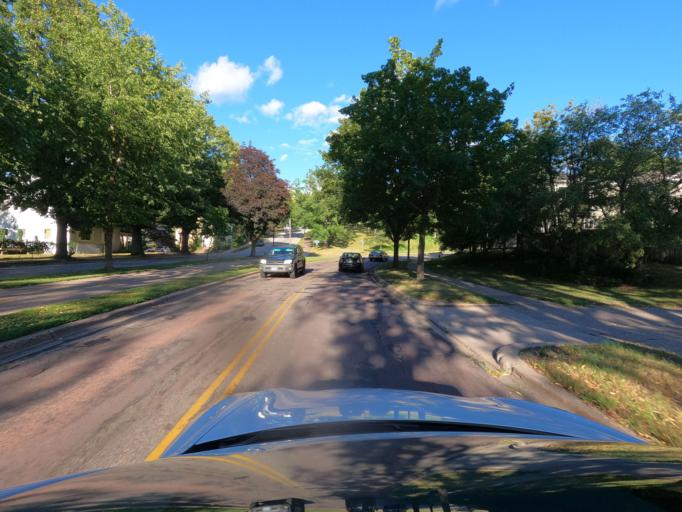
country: US
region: Minnesota
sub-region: Anoka County
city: Columbia Heights
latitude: 45.0257
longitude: -93.2455
